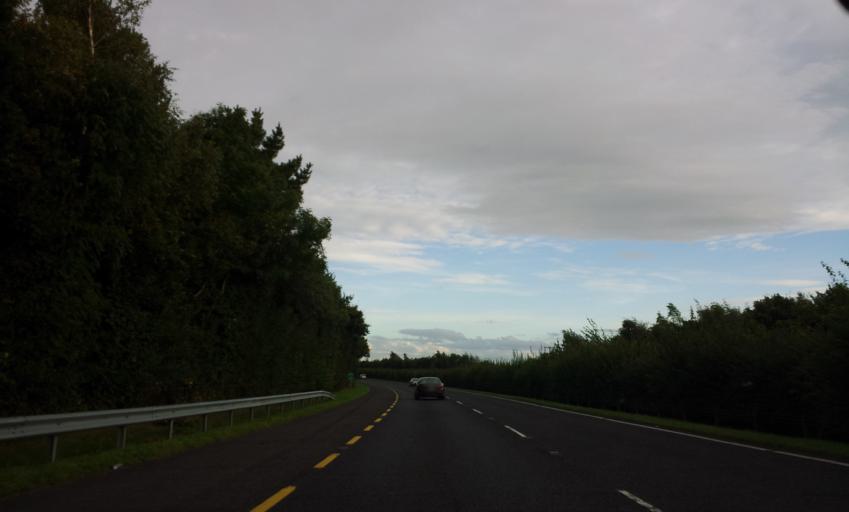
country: IE
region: Munster
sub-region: An Clar
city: Shannon
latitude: 52.6996
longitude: -8.8309
